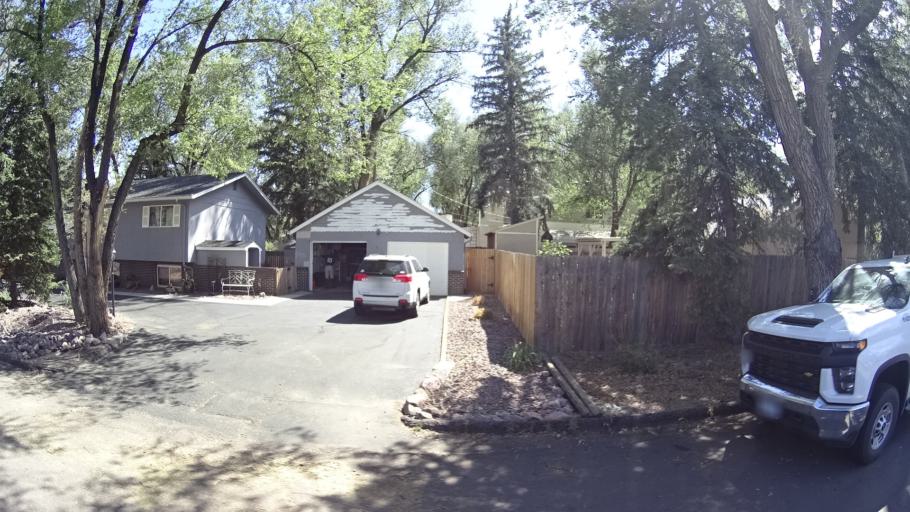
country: US
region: Colorado
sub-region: El Paso County
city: Colorado Springs
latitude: 38.8054
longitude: -104.8426
